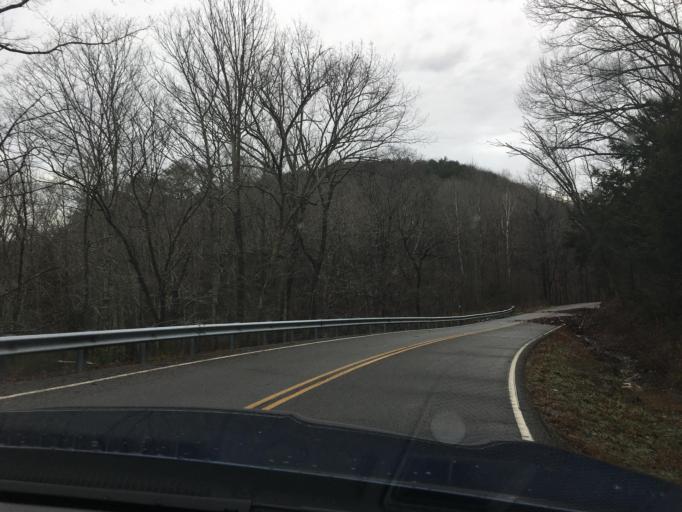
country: US
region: Tennessee
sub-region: McMinn County
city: Englewood
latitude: 35.3571
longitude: -84.4208
